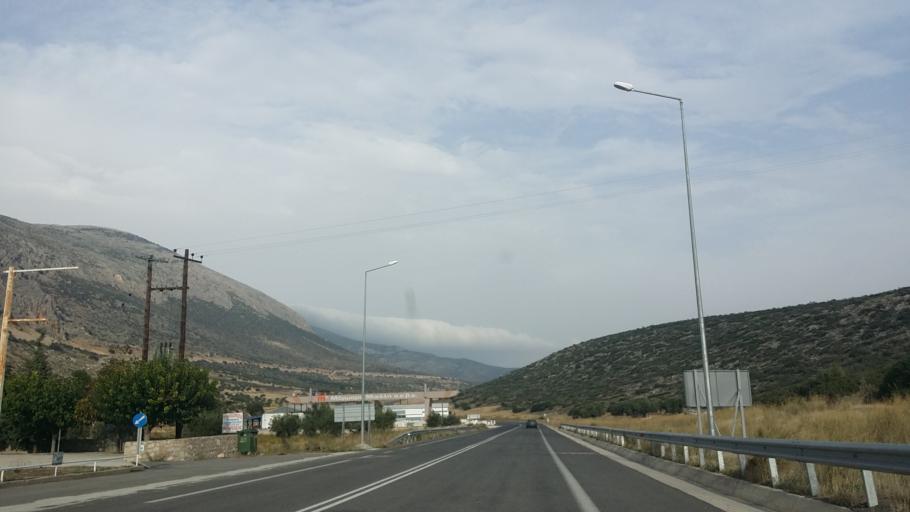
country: GR
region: Central Greece
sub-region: Nomos Voiotias
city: Korini
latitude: 38.2551
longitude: 22.9946
